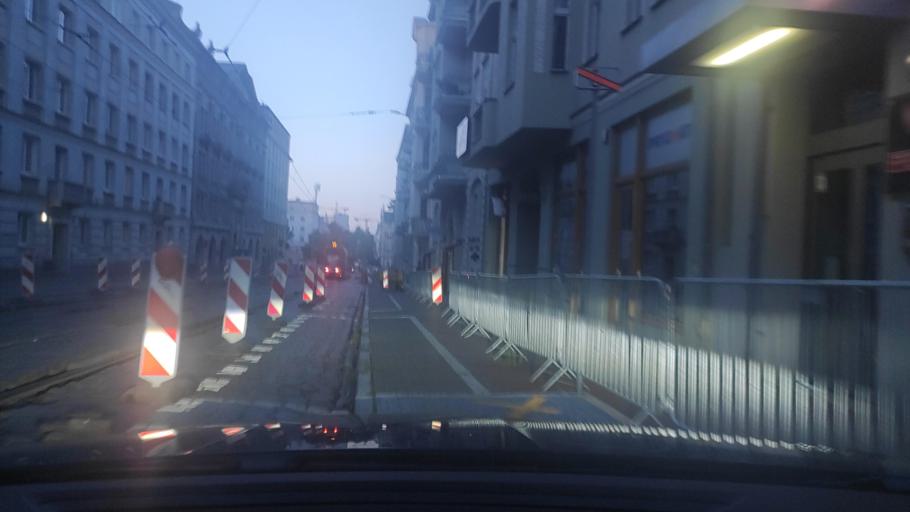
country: PL
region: Greater Poland Voivodeship
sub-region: Poznan
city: Poznan
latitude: 52.4086
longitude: 16.9222
